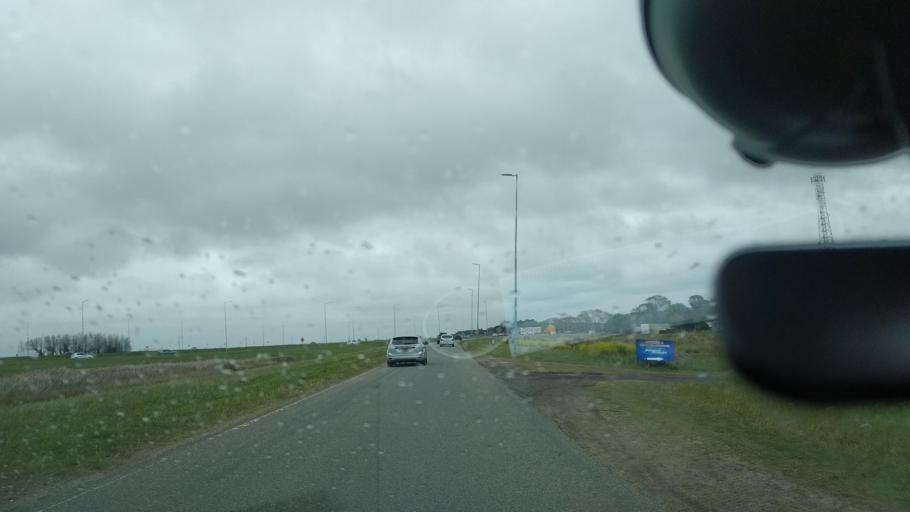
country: AR
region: Buenos Aires
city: San Clemente del Tuyu
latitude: -36.3884
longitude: -56.7384
